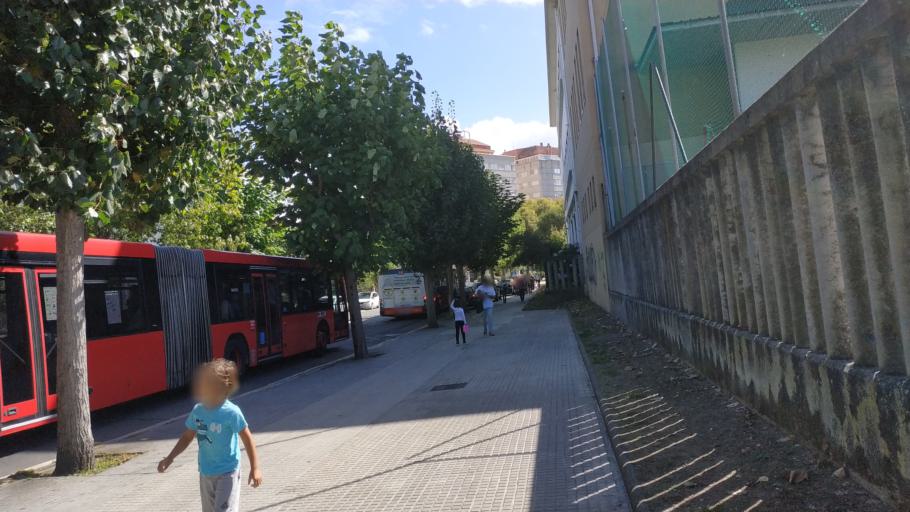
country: ES
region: Galicia
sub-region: Provincia da Coruna
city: A Coruna
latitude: 43.3707
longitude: -8.4214
